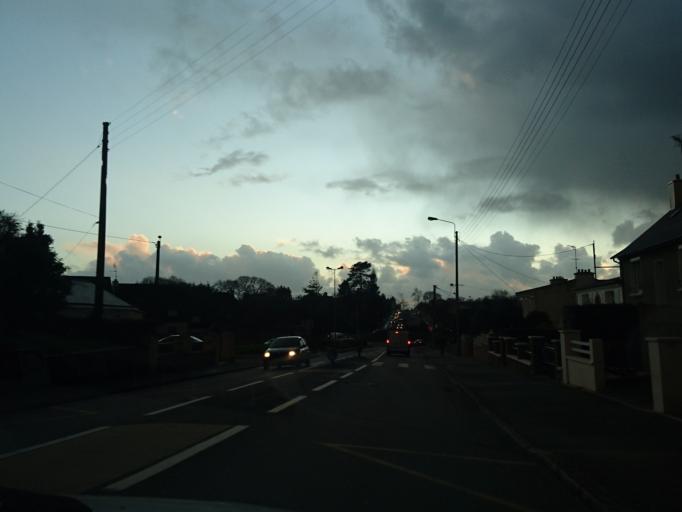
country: FR
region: Brittany
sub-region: Departement du Finistere
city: Guipavas
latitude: 48.4291
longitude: -4.4106
